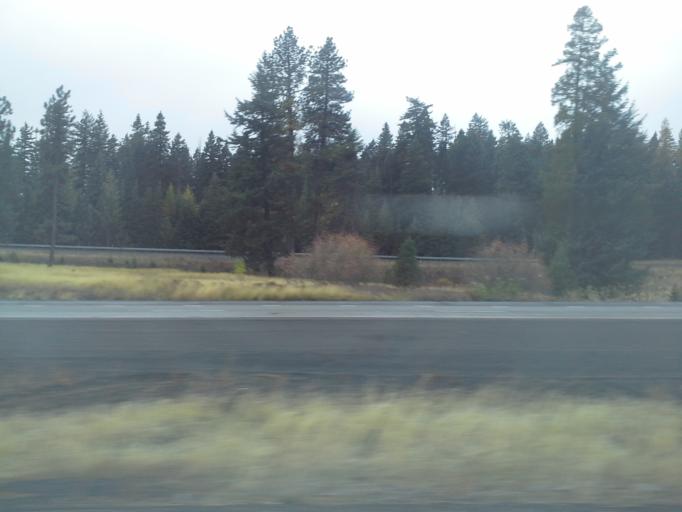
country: US
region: Oregon
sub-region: Umatilla County
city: Mission
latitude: 45.5389
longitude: -118.4577
